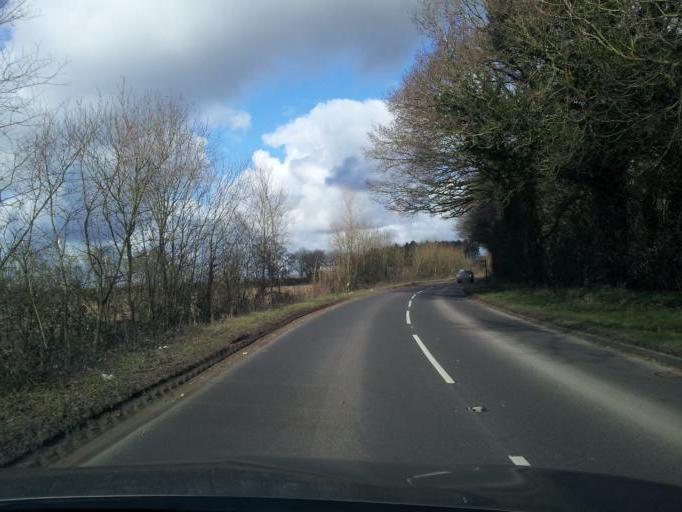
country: GB
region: England
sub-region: Norfolk
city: Mattishall
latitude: 52.6730
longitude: 1.0996
